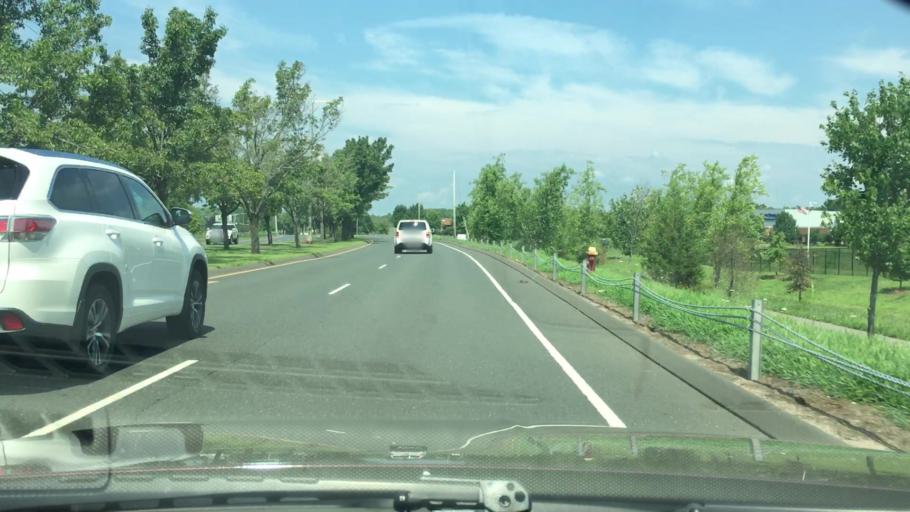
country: US
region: Connecticut
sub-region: Hartford County
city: Windsor
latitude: 41.8771
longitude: -72.6973
